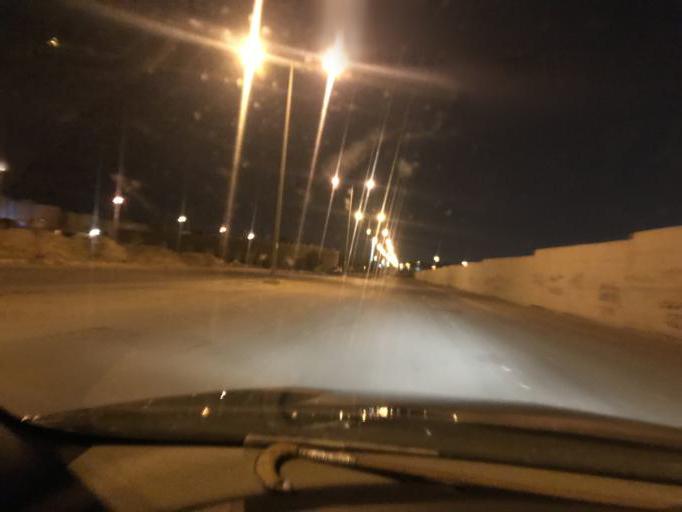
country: SA
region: Ar Riyad
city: Riyadh
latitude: 24.8153
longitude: 46.7165
